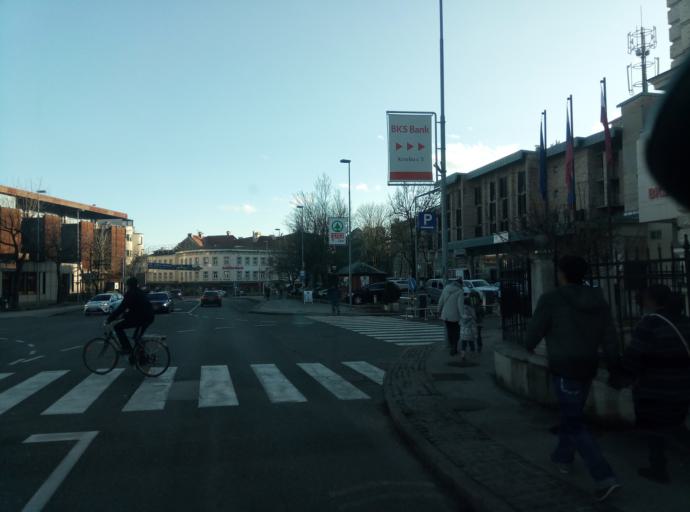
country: SI
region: Kranj
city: Kranj
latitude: 46.2428
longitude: 14.3550
